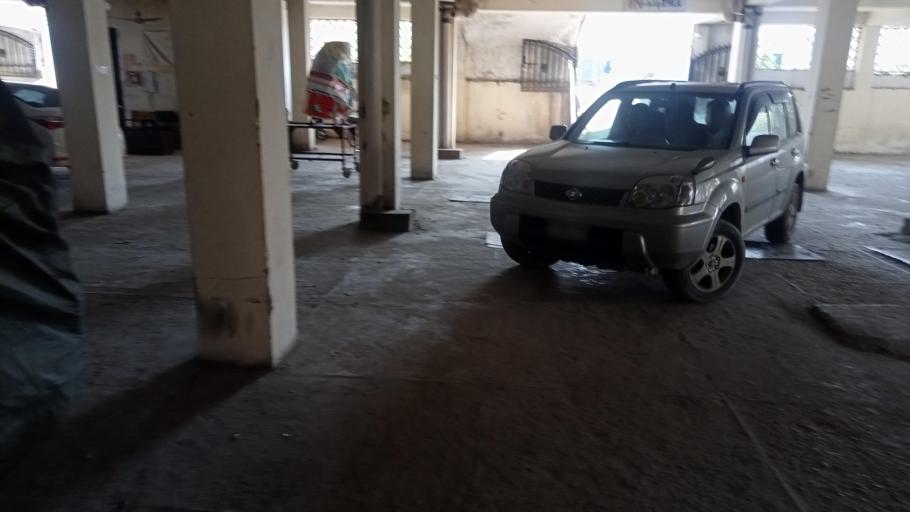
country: PK
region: Khyber Pakhtunkhwa
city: Mingora
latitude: 34.7697
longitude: 72.3597
